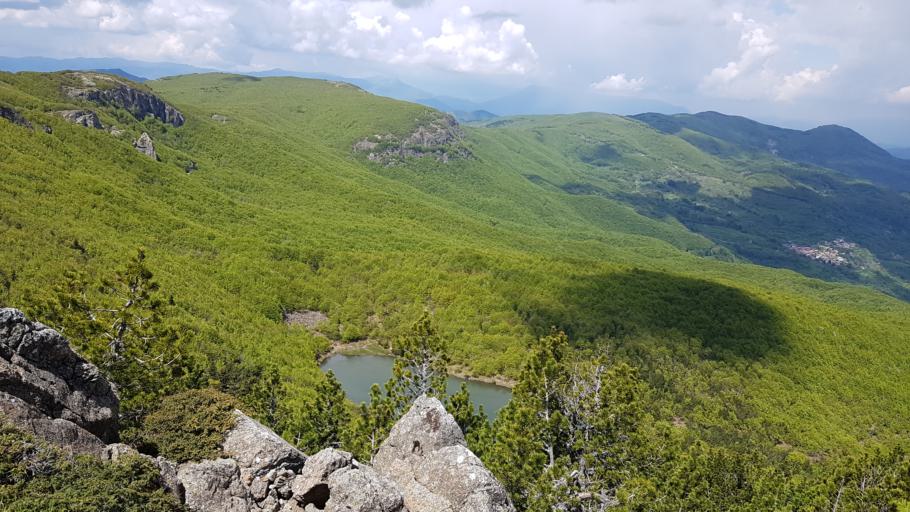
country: IT
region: Liguria
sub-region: Provincia di Genova
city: Santo Stefano d'Aveto
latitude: 44.5604
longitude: 9.5063
